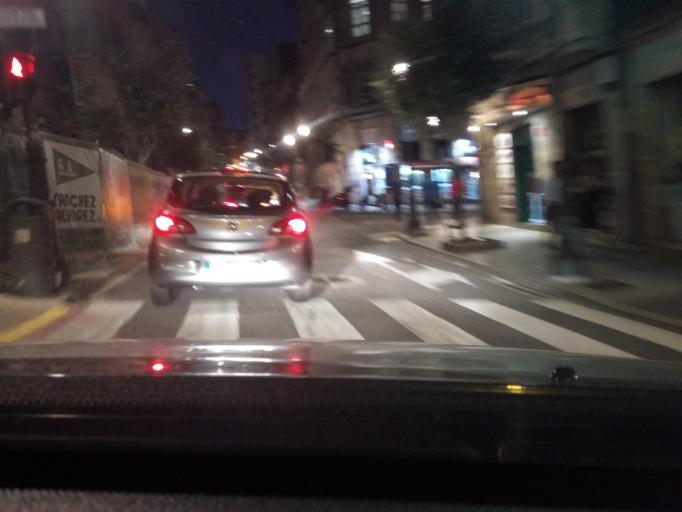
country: ES
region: Galicia
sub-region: Provincia de Pontevedra
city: Vigo
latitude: 42.2361
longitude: -8.7166
